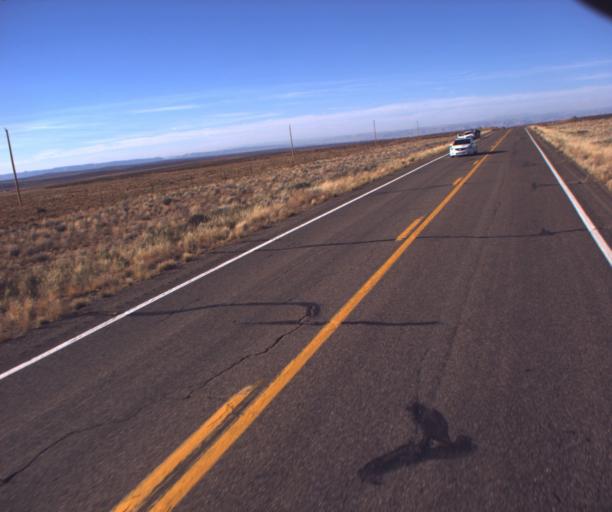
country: US
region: Arizona
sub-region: Coconino County
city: LeChee
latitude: 36.7298
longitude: -111.2822
